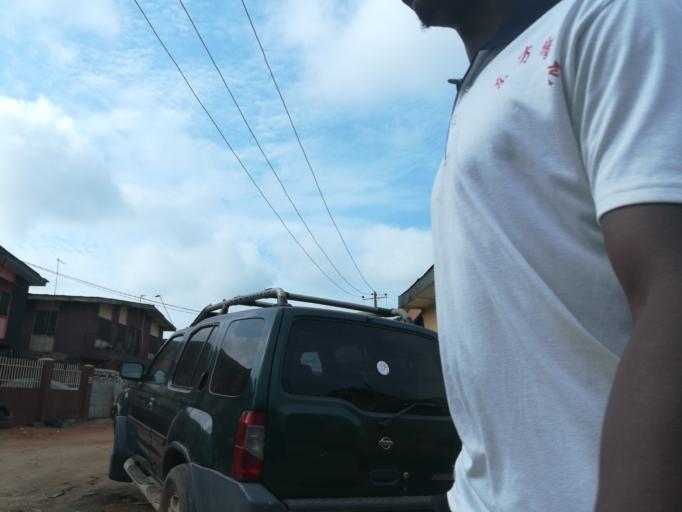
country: NG
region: Lagos
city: Agege
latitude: 6.6136
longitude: 3.3258
